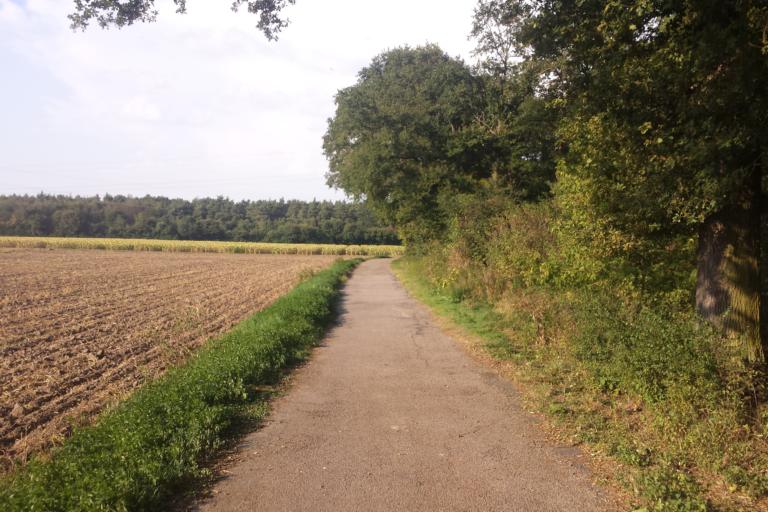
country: DE
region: Baden-Wuerttemberg
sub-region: Karlsruhe Region
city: Bruhl
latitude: 49.4308
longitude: 8.5569
